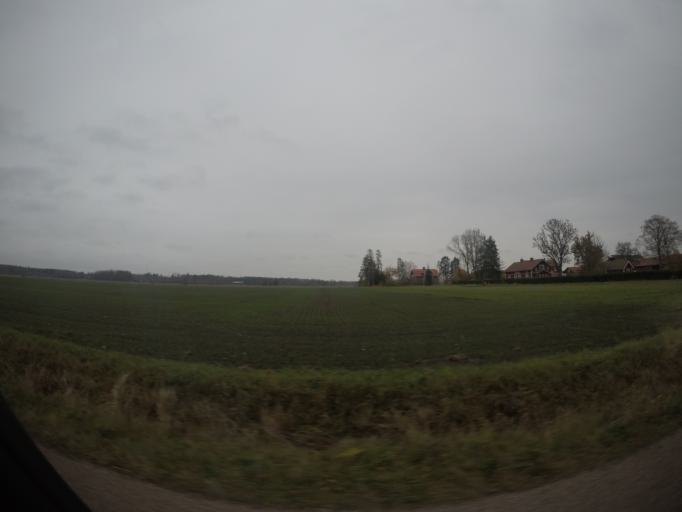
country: SE
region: Vaestmanland
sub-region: Kopings Kommun
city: Koping
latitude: 59.5596
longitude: 16.0957
